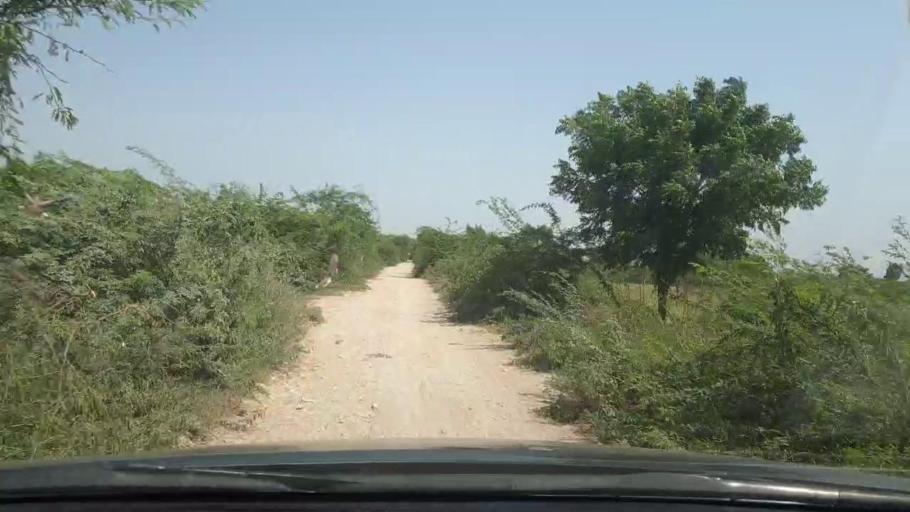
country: PK
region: Sindh
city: Naukot
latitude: 24.8132
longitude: 69.2606
